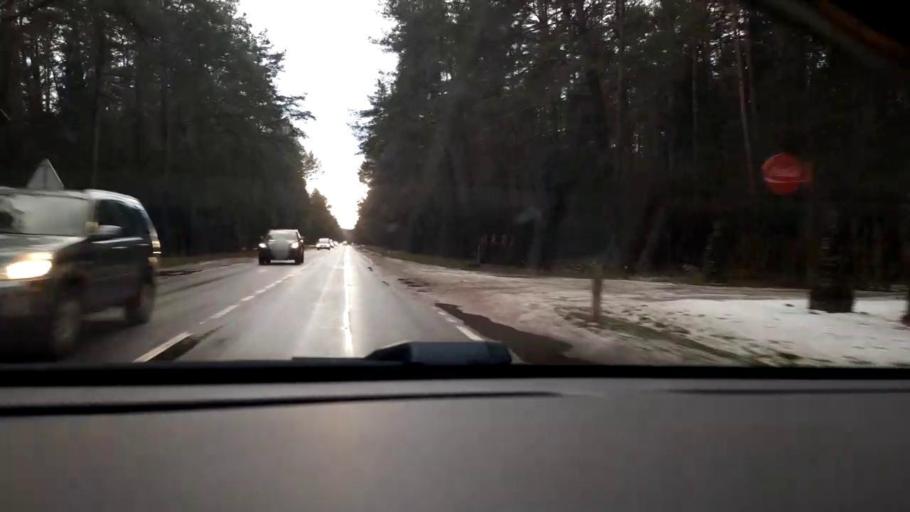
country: LT
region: Vilnius County
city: Rasos
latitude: 54.7712
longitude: 25.3814
